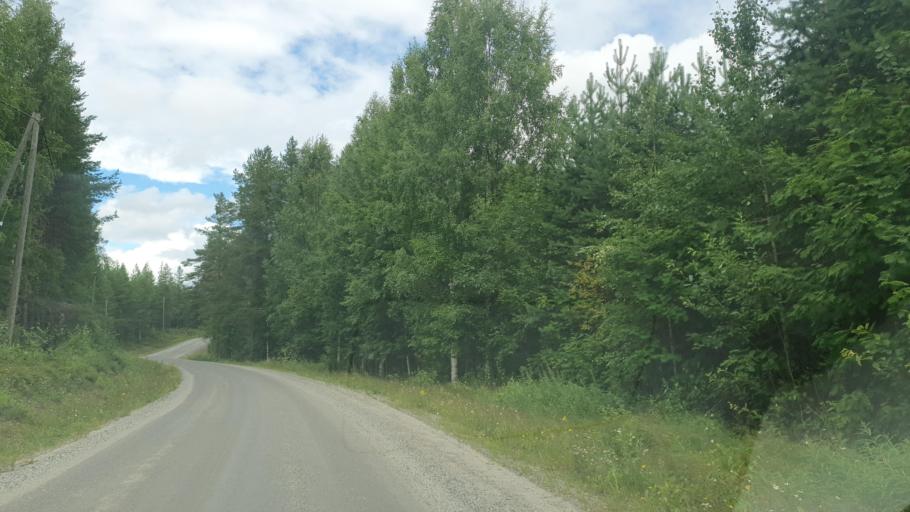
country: FI
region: Kainuu
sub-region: Kehys-Kainuu
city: Kuhmo
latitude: 64.1023
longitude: 29.4022
